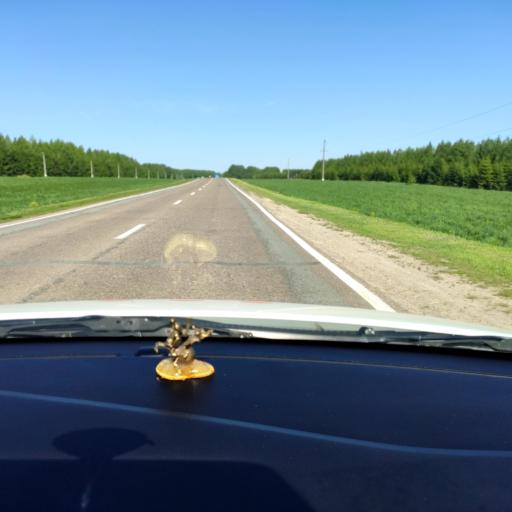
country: RU
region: Tatarstan
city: Vysokaya Gora
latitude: 56.0302
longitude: 49.2460
